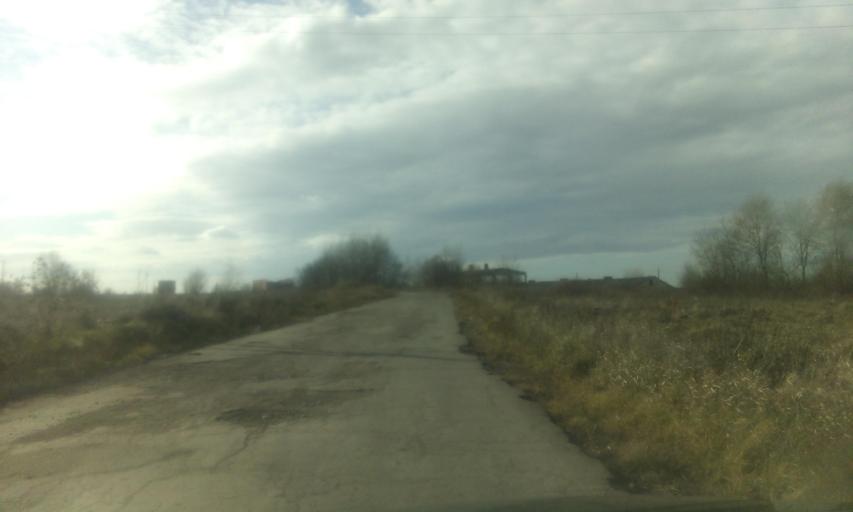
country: RU
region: Tula
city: Dubovka
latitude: 53.9421
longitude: 38.0334
